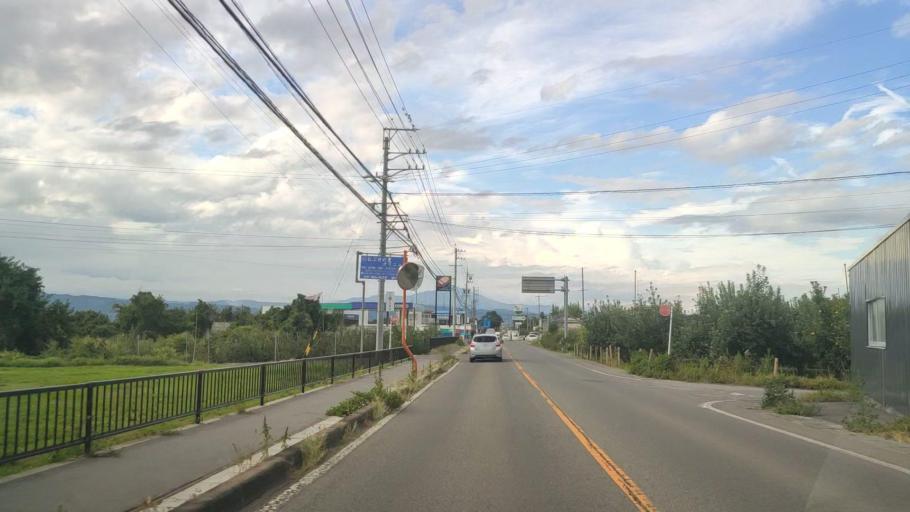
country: JP
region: Nagano
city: Suzaka
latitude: 36.6839
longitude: 138.3161
